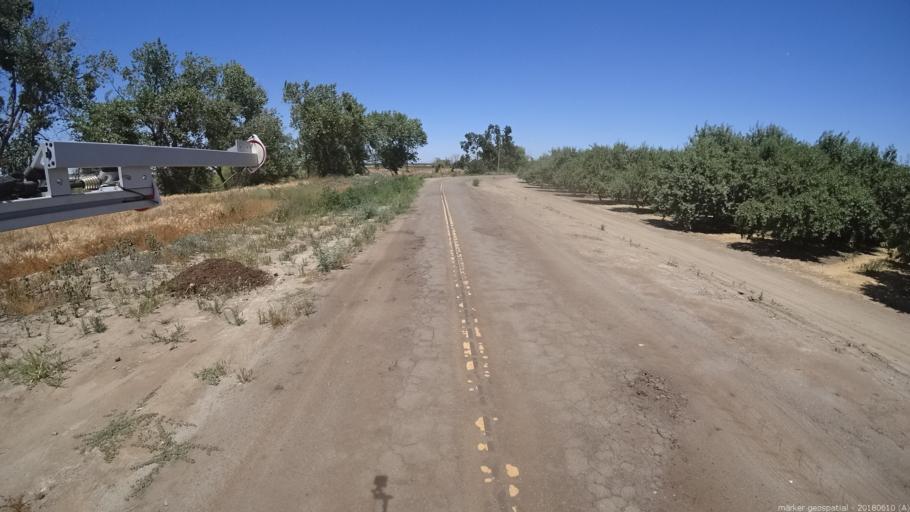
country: US
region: California
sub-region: Madera County
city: Chowchilla
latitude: 37.0644
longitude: -120.4005
